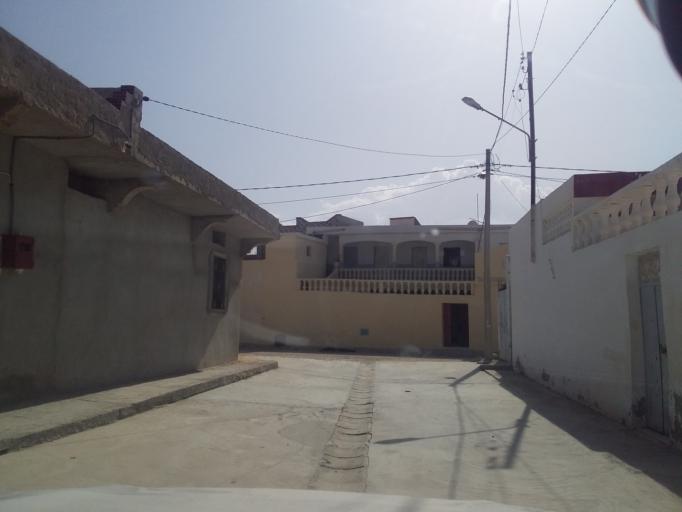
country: TN
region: Qabis
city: Gabes
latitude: 33.6234
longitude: 10.2861
